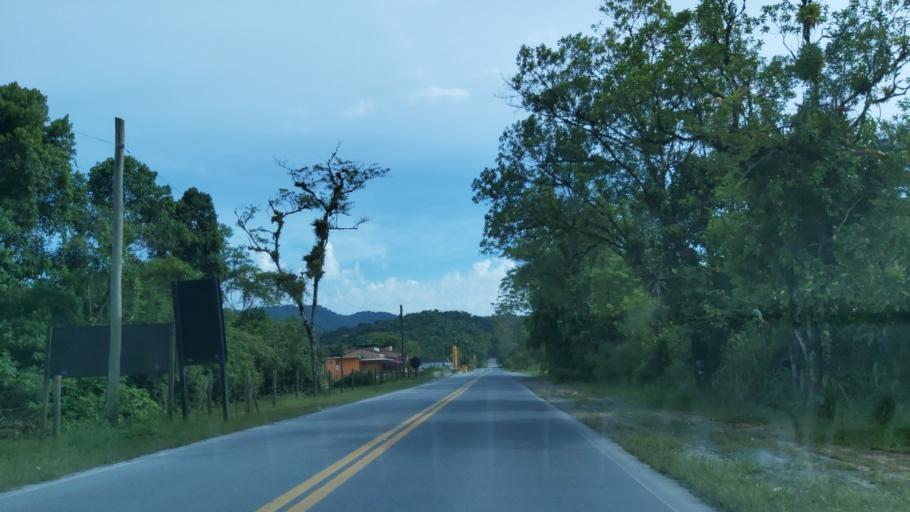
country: BR
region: Sao Paulo
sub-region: Miracatu
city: Miracatu
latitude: -24.0631
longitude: -47.5907
